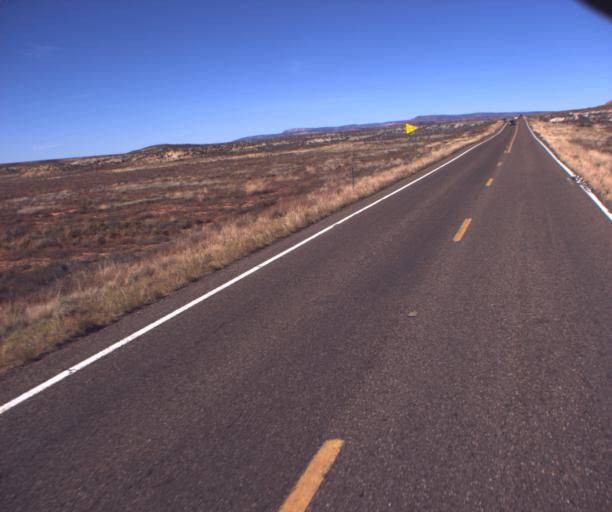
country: US
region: Arizona
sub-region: Coconino County
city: Fredonia
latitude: 36.9265
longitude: -112.4726
